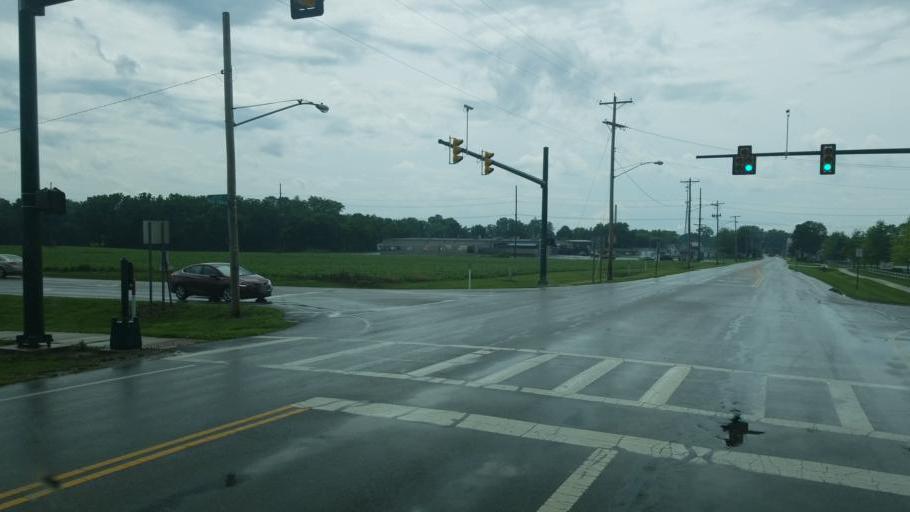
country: US
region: Ohio
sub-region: Knox County
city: Mount Vernon
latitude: 40.3844
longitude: -82.4781
